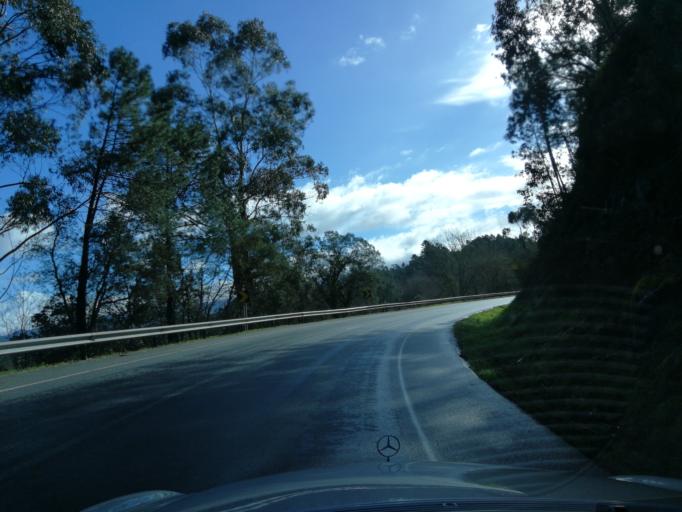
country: PT
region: Viana do Castelo
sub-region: Ponte da Barca
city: Ponte da Barca
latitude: 41.8114
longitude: -8.3471
